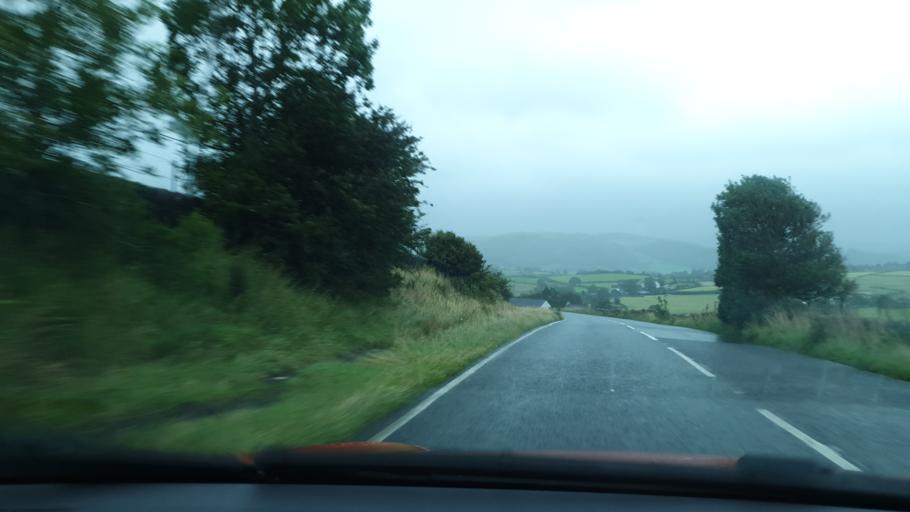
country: GB
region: England
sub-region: Cumbria
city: Ulverston
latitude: 54.2557
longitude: -3.1150
